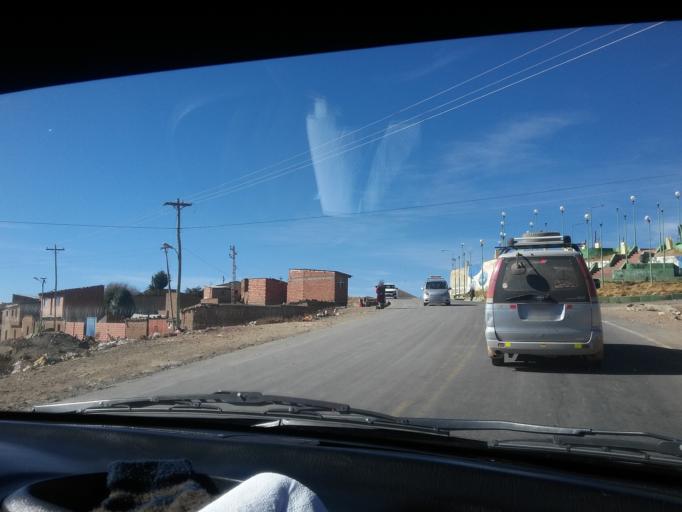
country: BO
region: Potosi
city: Llallagua
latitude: -18.4181
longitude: -66.5842
